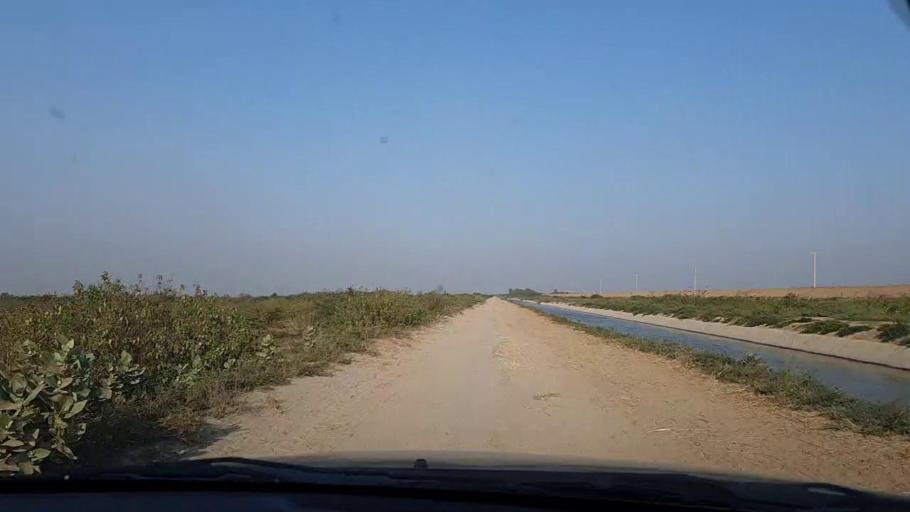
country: PK
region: Sindh
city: Chuhar Jamali
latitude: 24.2818
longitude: 67.7438
